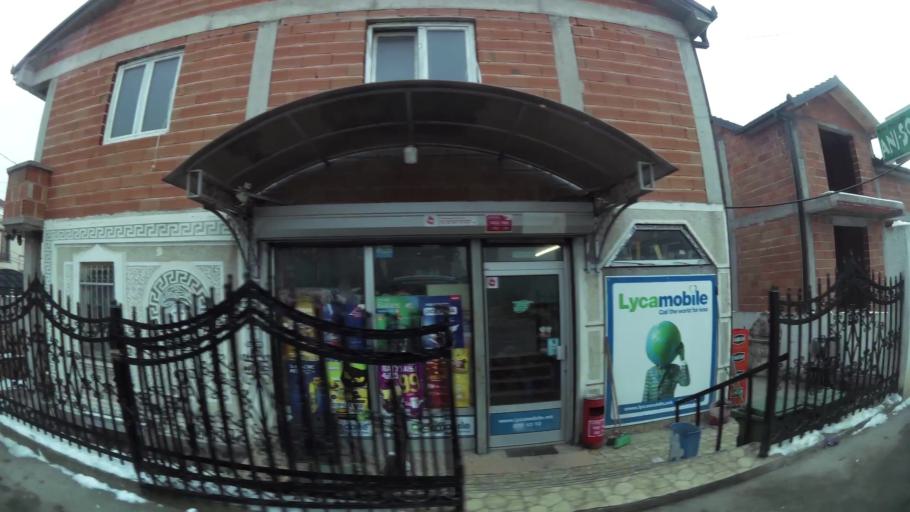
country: MK
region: Suto Orizari
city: Suto Orizare
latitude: 42.0403
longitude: 21.4289
